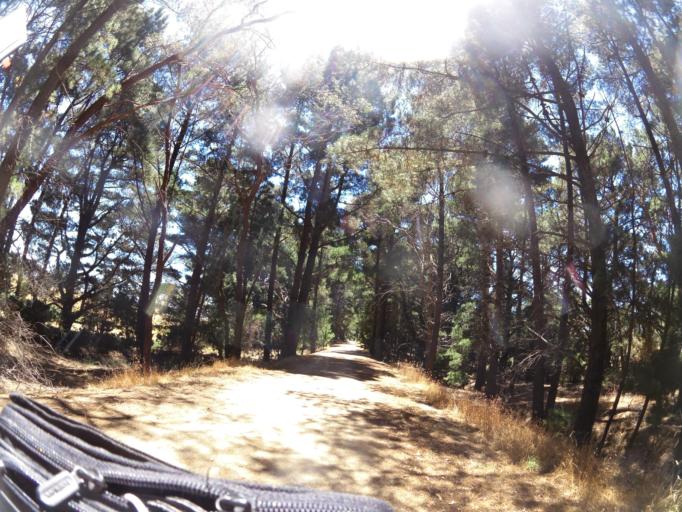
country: AU
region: Victoria
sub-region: Ballarat North
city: Delacombe
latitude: -37.5863
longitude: 143.7237
